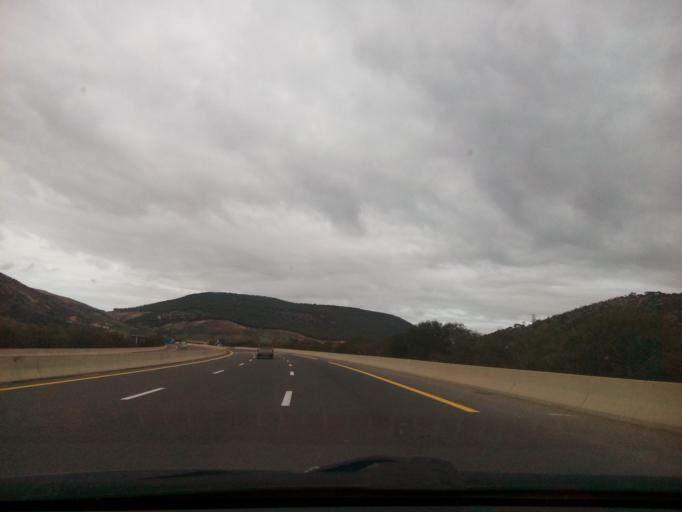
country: DZ
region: Sidi Bel Abbes
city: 'Ain el Berd
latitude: 35.3707
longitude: -0.4995
